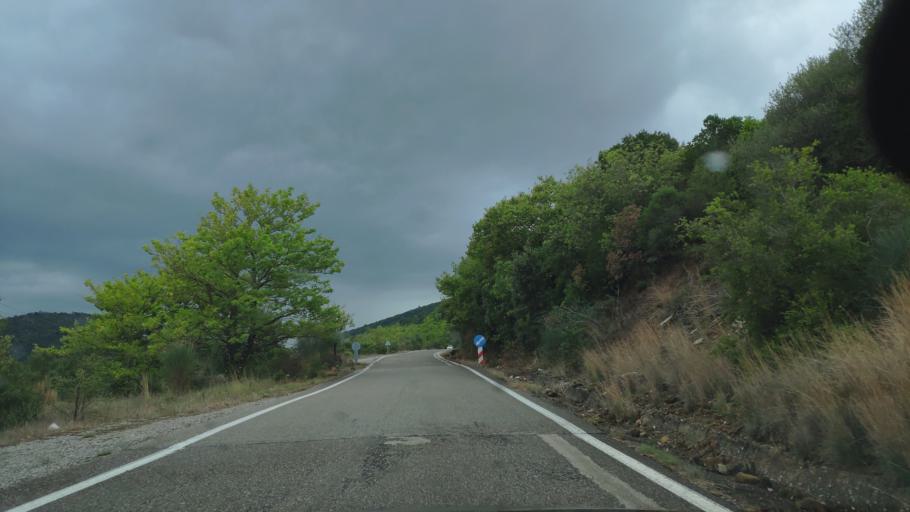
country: GR
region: West Greece
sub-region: Nomos Aitolias kai Akarnanias
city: Lepenou
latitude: 38.8116
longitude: 21.3342
